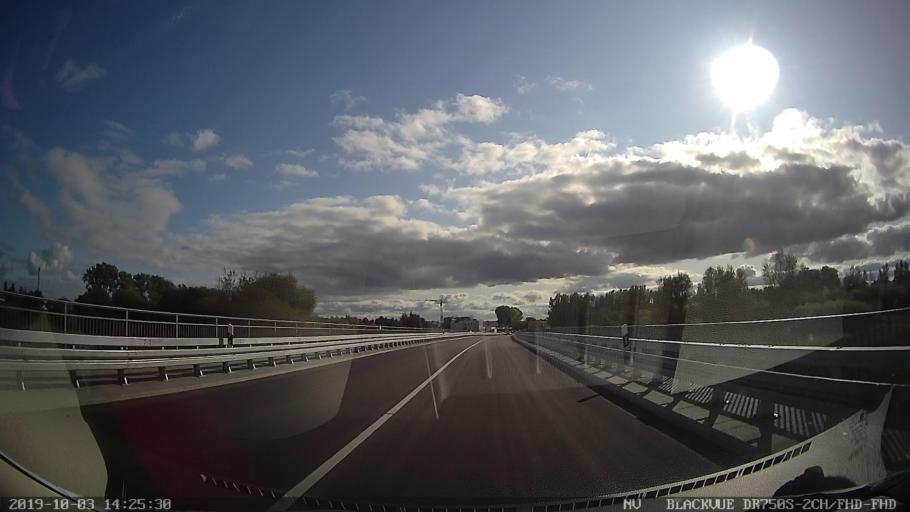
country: DE
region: Schleswig-Holstein
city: Pinneberg
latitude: 53.6616
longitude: 9.7760
